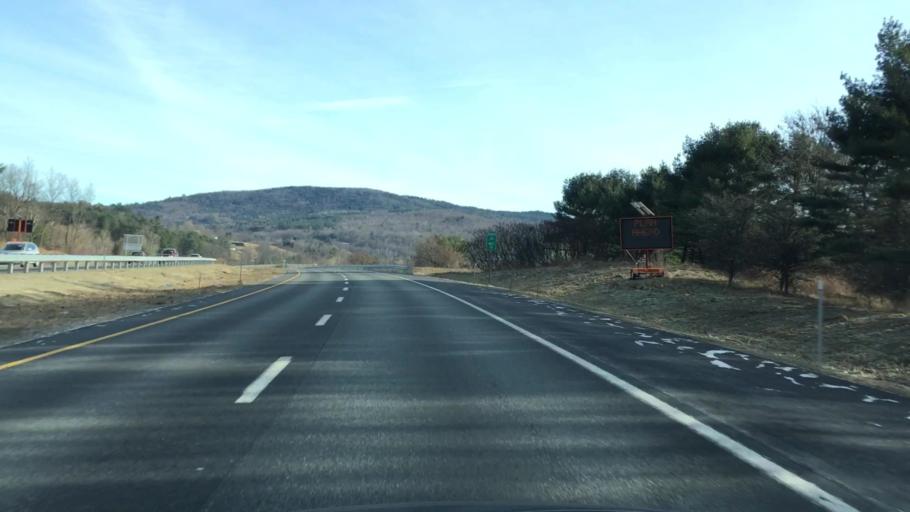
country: US
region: New Hampshire
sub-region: Grafton County
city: Lebanon
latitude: 43.6412
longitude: -72.2261
